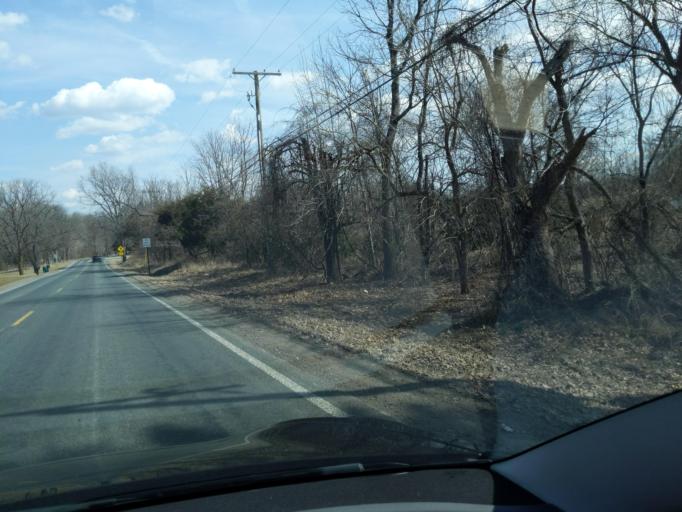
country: US
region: Michigan
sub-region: Washtenaw County
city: Chelsea
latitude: 42.3840
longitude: -84.0137
